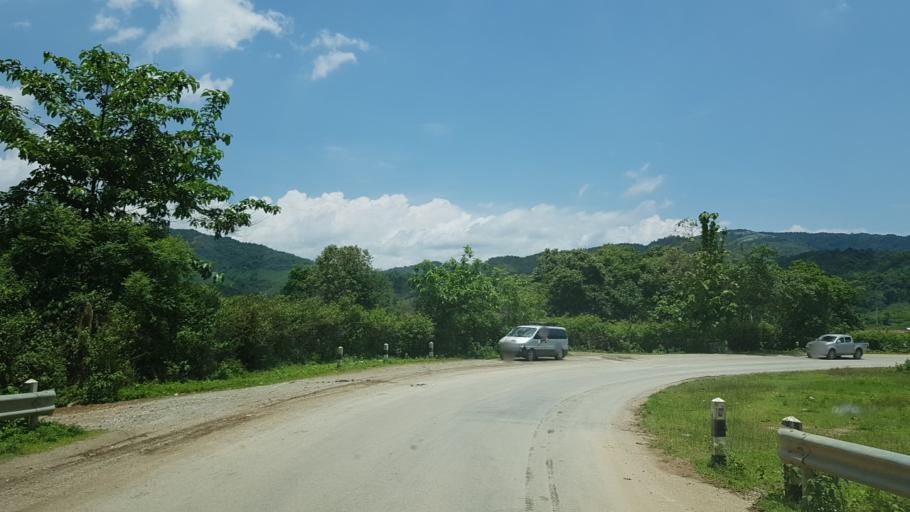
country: LA
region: Vientiane
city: Muang Kasi
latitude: 19.2749
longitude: 102.2170
